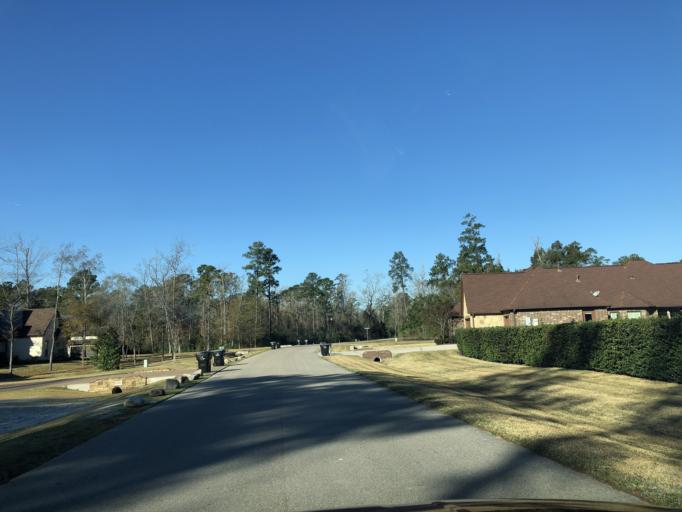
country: US
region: Texas
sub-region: Montgomery County
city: Porter Heights
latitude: 30.0686
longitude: -95.3267
